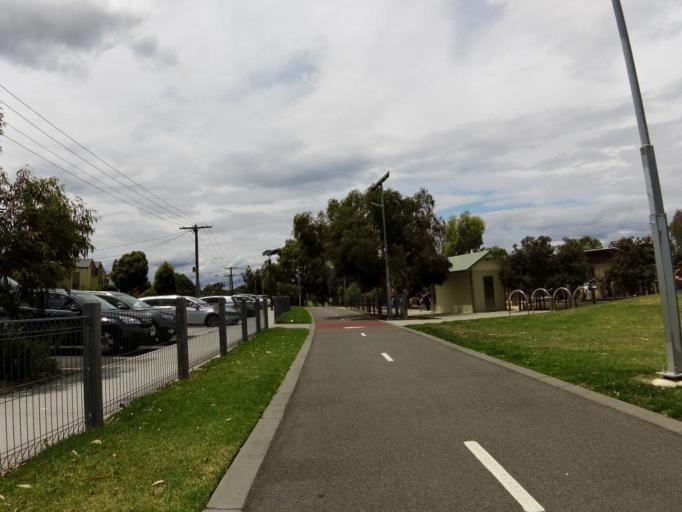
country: AU
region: Victoria
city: Ashburton
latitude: -37.8712
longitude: 145.0848
